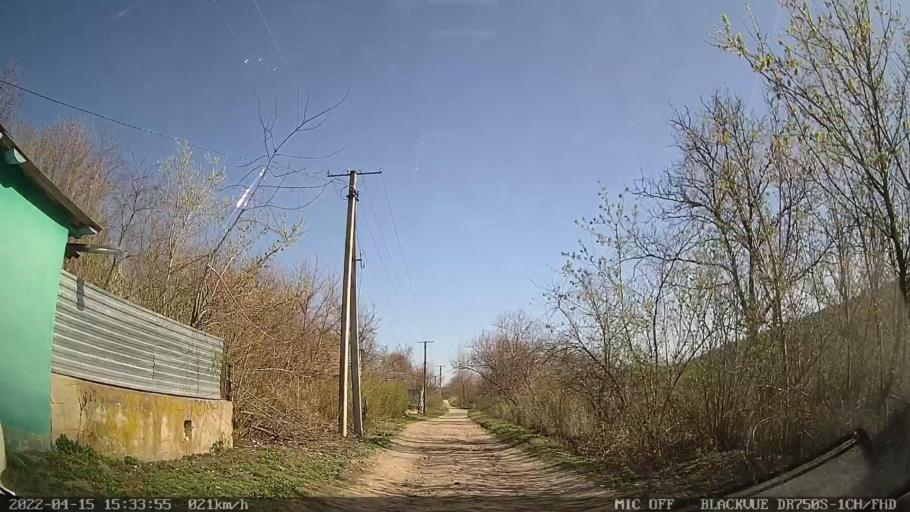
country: MD
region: Raionul Ocnita
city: Otaci
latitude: 48.3486
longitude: 27.9252
